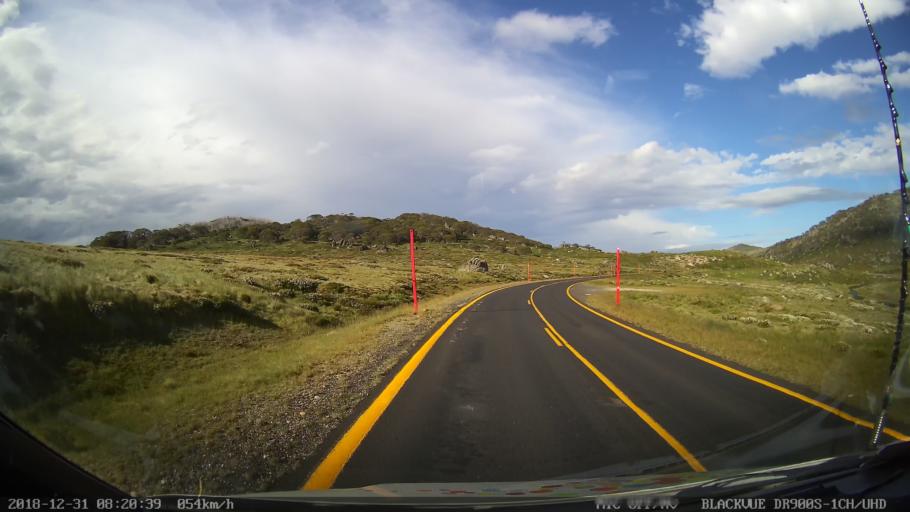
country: AU
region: New South Wales
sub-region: Snowy River
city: Jindabyne
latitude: -36.4257
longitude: 148.3743
